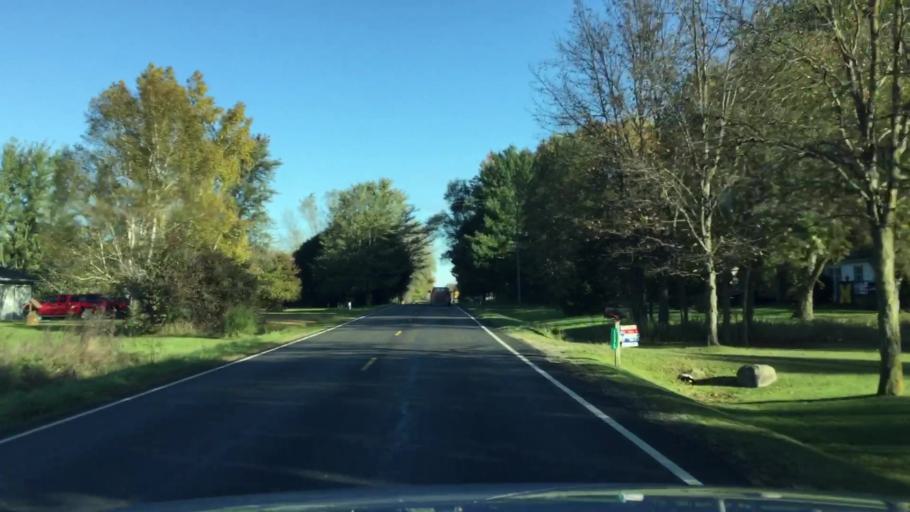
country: US
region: Michigan
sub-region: Shiawassee County
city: Durand
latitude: 42.8420
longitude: -83.9453
